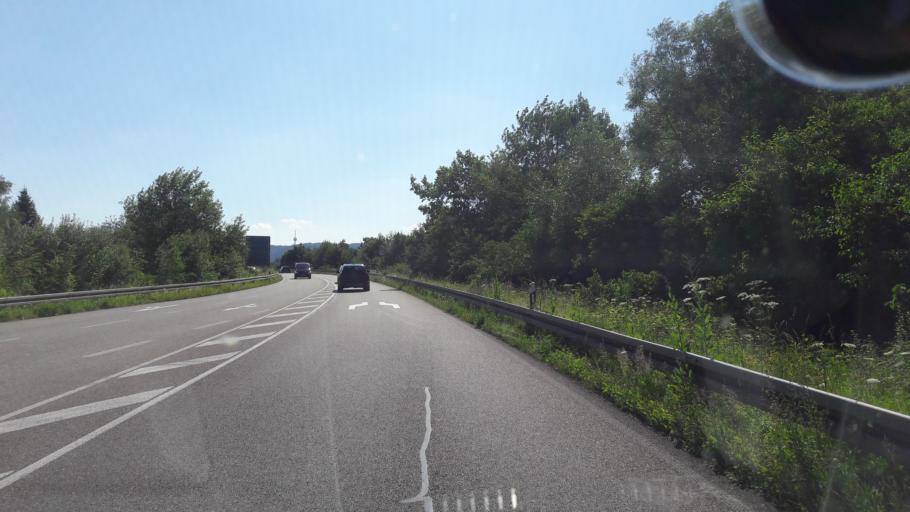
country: DE
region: Baden-Wuerttemberg
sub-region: Karlsruhe Region
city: Ettlingen
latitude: 48.9560
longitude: 8.3864
